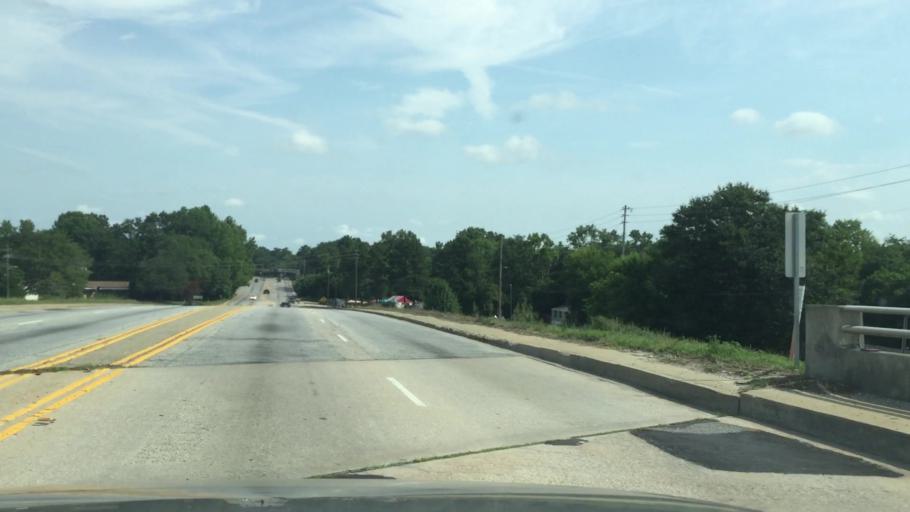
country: US
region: South Carolina
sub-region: Sumter County
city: South Sumter
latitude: 33.9064
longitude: -80.3538
